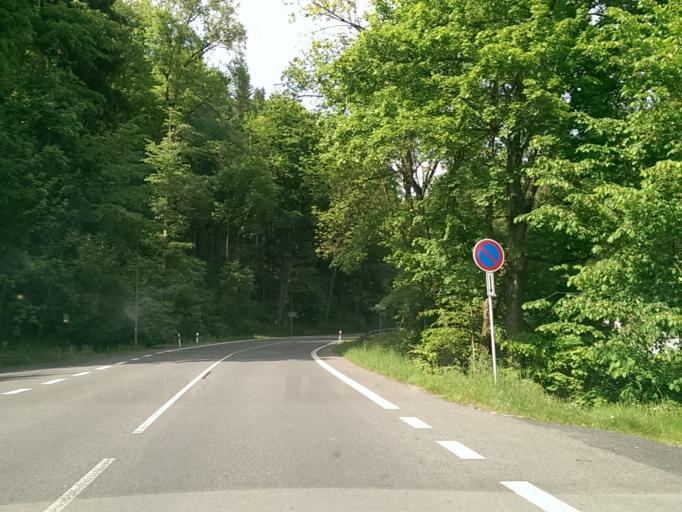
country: CZ
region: Liberecky
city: Zelezny Brod
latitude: 50.6480
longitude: 15.2555
